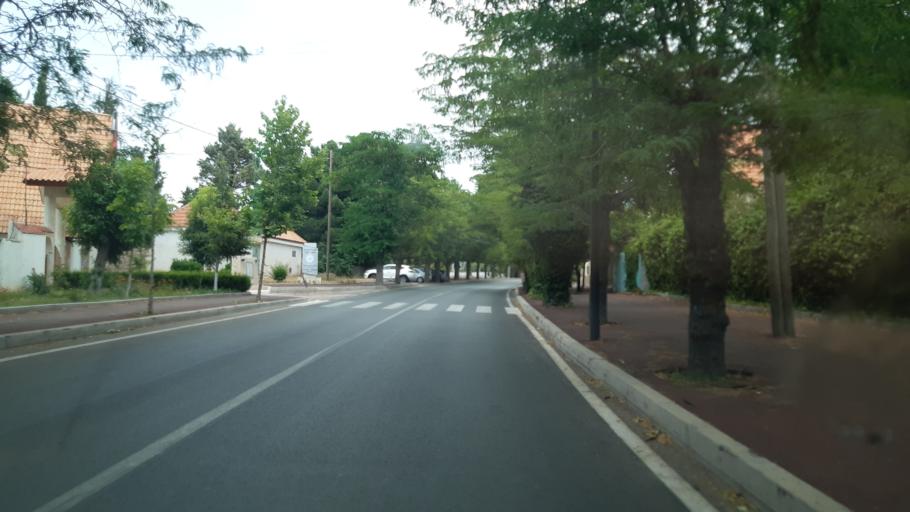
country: MA
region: Meknes-Tafilalet
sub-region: Ifrane
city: Ifrane
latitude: 33.5231
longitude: -5.1119
